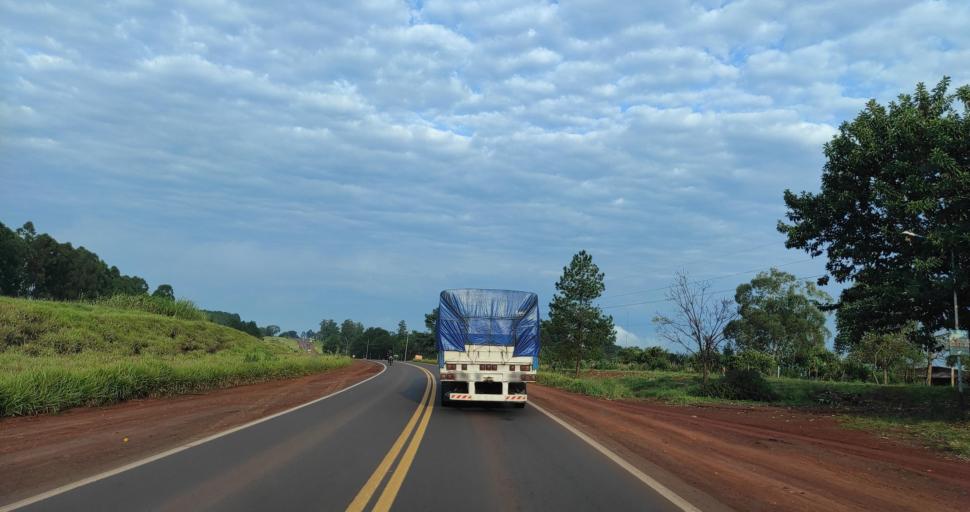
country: AR
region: Corrientes
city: Gobernador Ingeniero Valentin Virasoro
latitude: -27.9399
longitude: -55.9812
